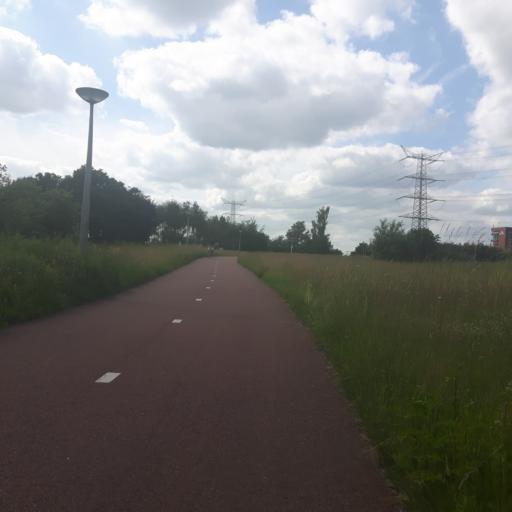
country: NL
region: Overijssel
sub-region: Gemeente Enschede
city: Enschede
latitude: 52.1992
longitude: 6.8948
